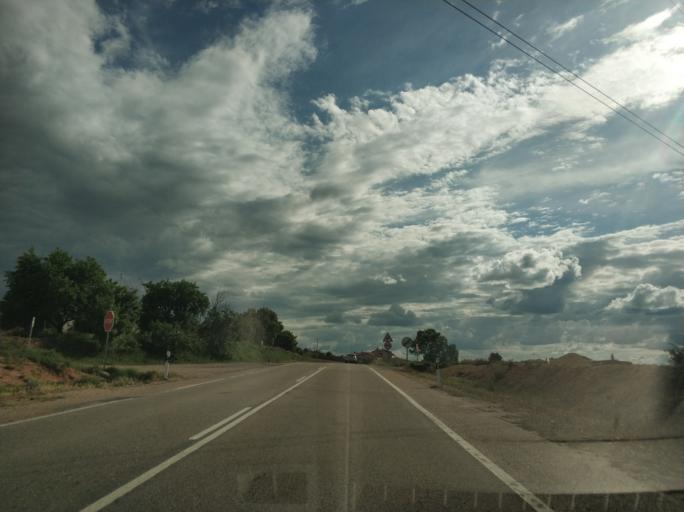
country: ES
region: Castille and Leon
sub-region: Provincia de Burgos
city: Castrillo de la Vega
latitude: 41.6547
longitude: -3.7723
